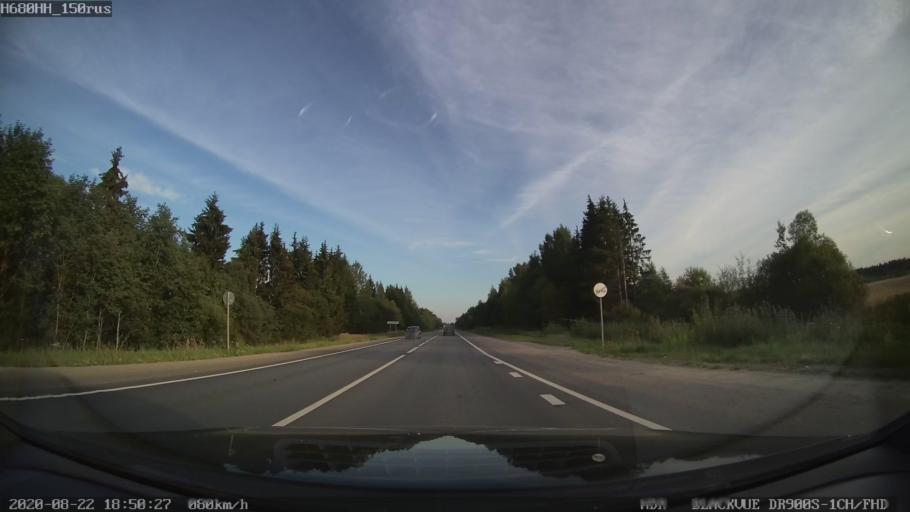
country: RU
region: Tverskaya
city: Rameshki
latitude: 57.2665
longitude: 36.0745
